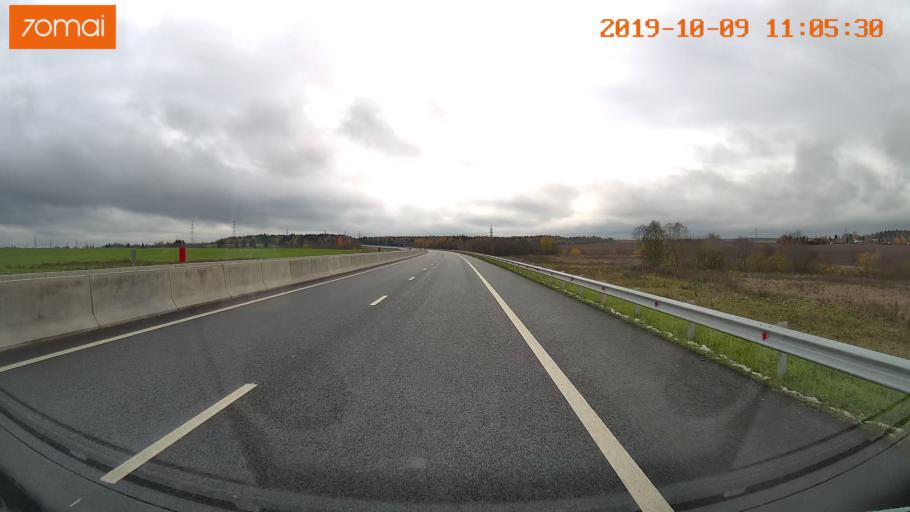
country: RU
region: Vologda
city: Molochnoye
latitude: 59.1992
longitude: 39.7582
